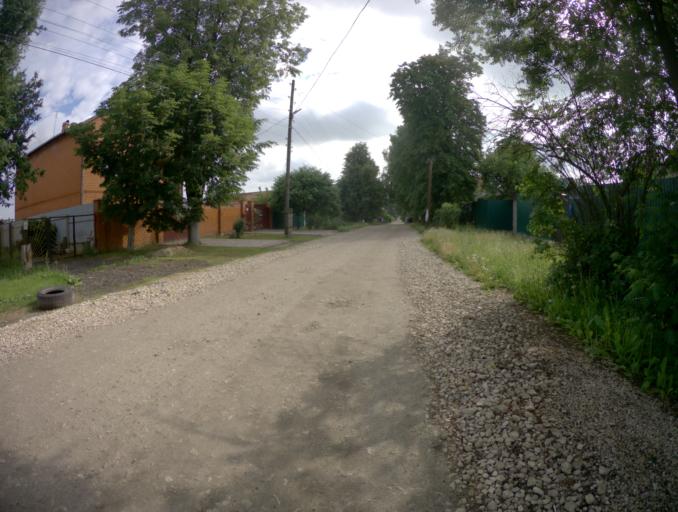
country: RU
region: Vladimir
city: Lakinsk
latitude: 56.0238
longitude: 39.9811
